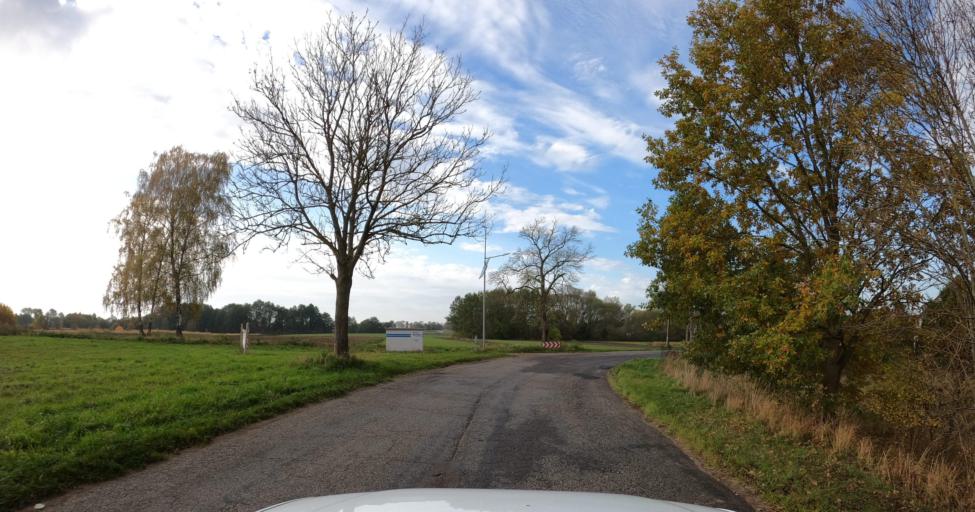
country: PL
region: West Pomeranian Voivodeship
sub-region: Powiat kamienski
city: Kamien Pomorski
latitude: 53.9627
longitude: 14.8324
